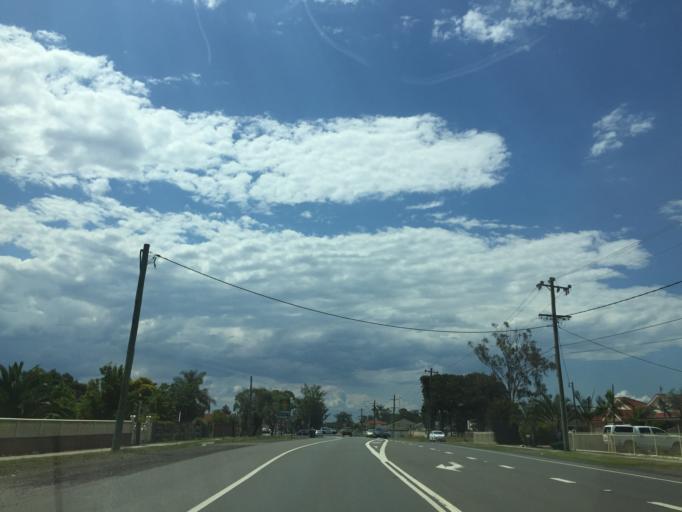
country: AU
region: New South Wales
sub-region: Blacktown
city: Glendenning
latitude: -33.7460
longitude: 150.8423
